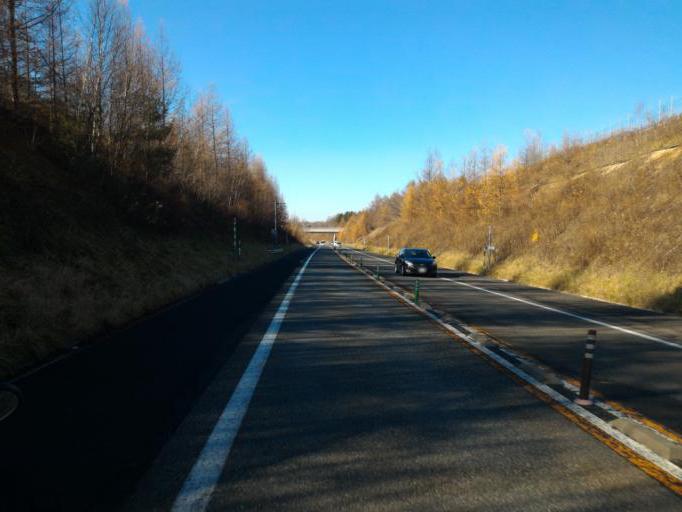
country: JP
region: Hokkaido
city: Chitose
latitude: 42.8966
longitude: 141.8576
